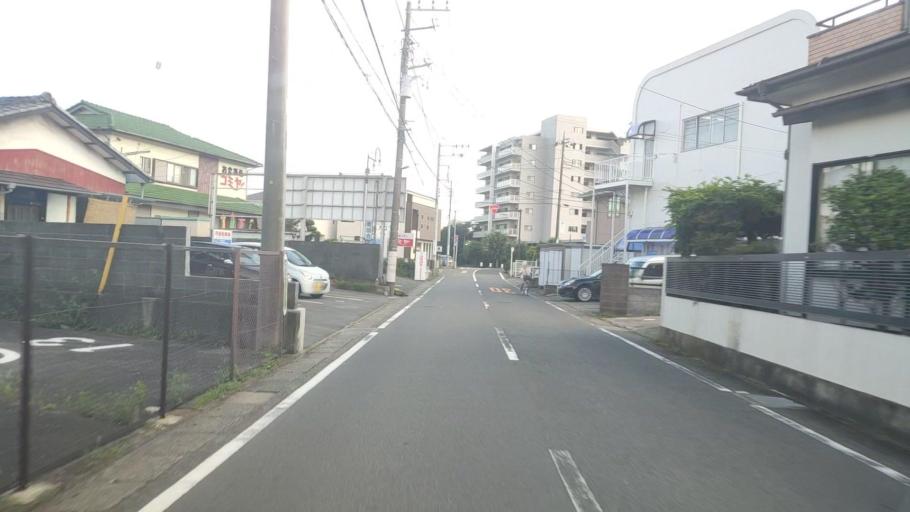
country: JP
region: Kanagawa
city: Hiratsuka
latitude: 35.3368
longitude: 139.3237
